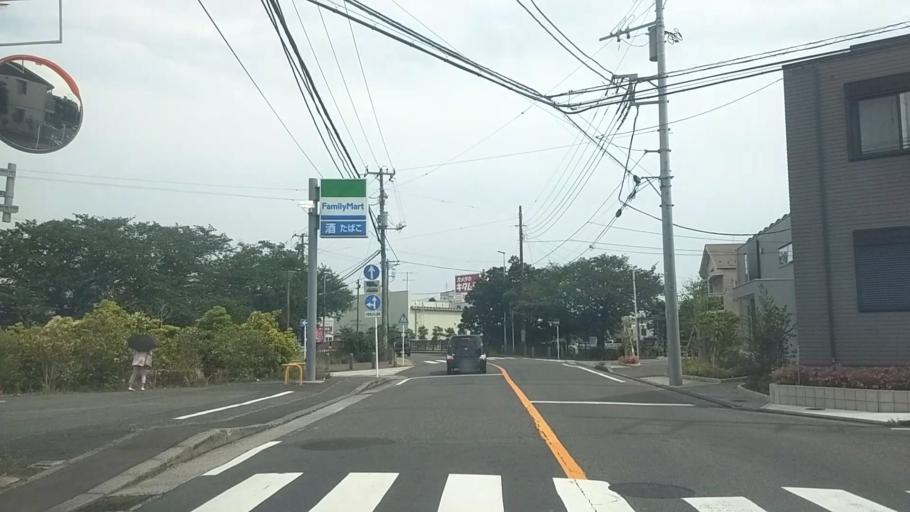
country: JP
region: Kanagawa
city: Fujisawa
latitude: 35.3919
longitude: 139.4602
